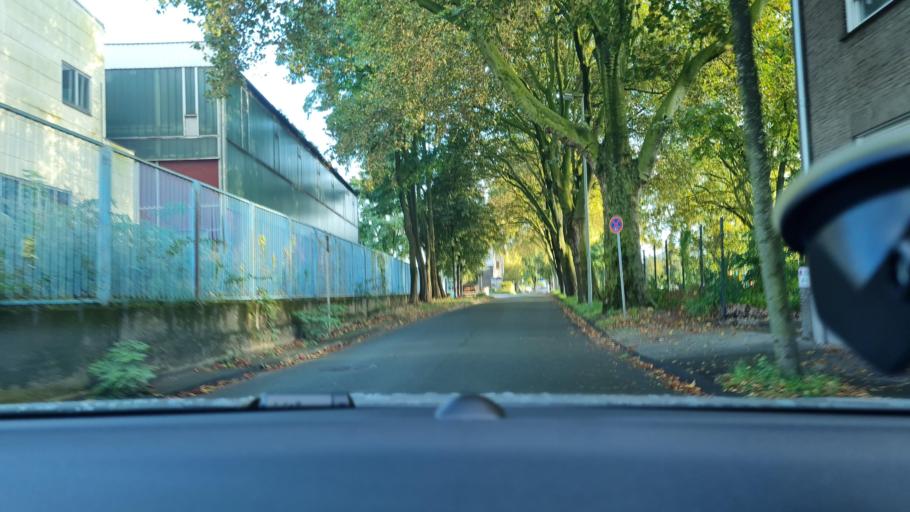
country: DE
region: North Rhine-Westphalia
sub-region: Regierungsbezirk Dusseldorf
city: Dinslaken
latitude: 51.5585
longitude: 6.7489
